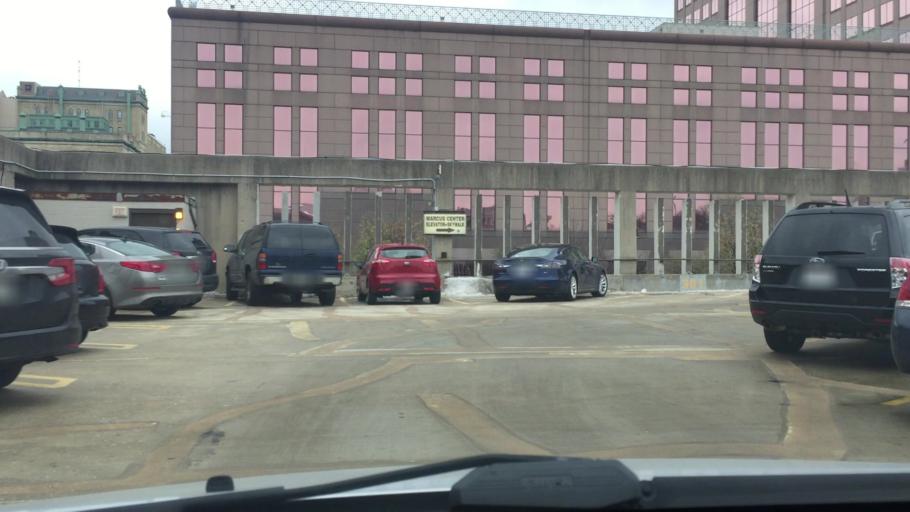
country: US
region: Wisconsin
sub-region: Milwaukee County
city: Milwaukee
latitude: 43.0444
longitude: -87.9116
